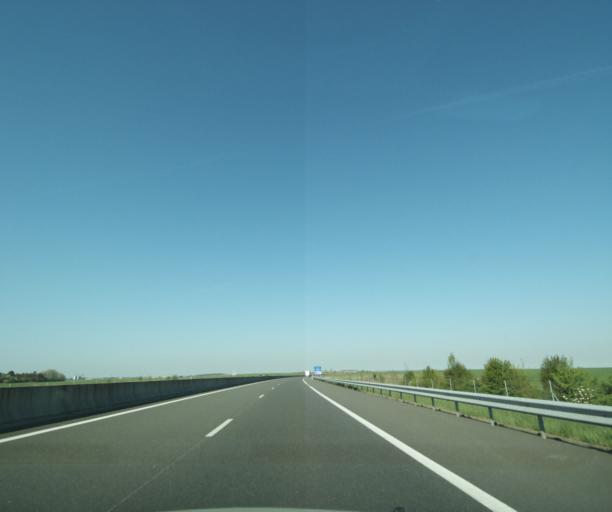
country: FR
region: Centre
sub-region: Departement du Loiret
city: Puiseaux
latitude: 48.0928
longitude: 2.0928
